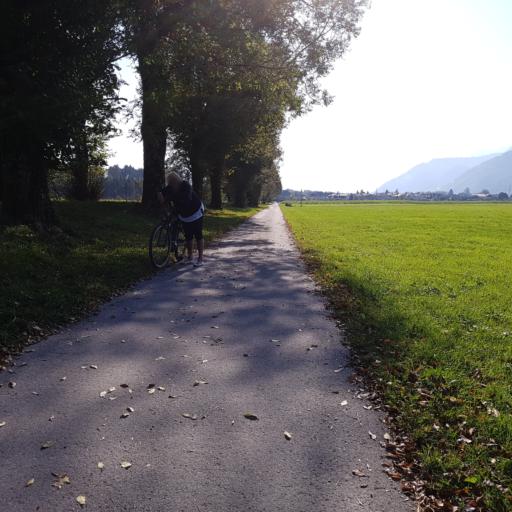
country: AT
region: Salzburg
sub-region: Politischer Bezirk Hallein
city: Puch bei Hallein
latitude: 47.7173
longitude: 13.0719
